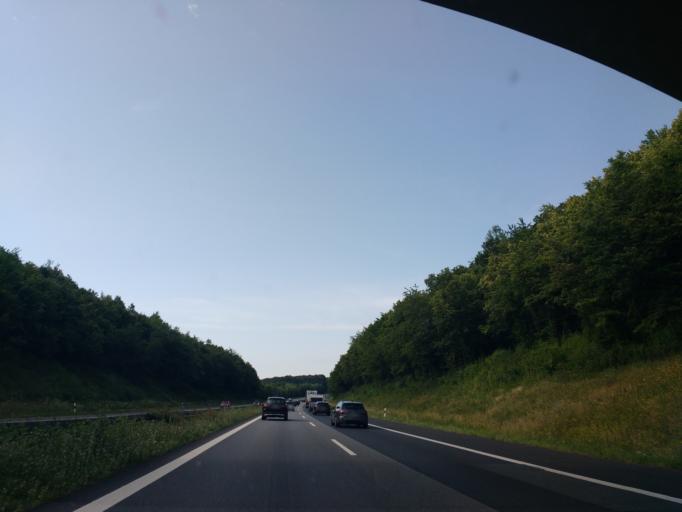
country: DE
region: Bavaria
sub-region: Regierungsbezirk Unterfranken
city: Unterpleichfeld
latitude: 49.8933
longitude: 10.0009
